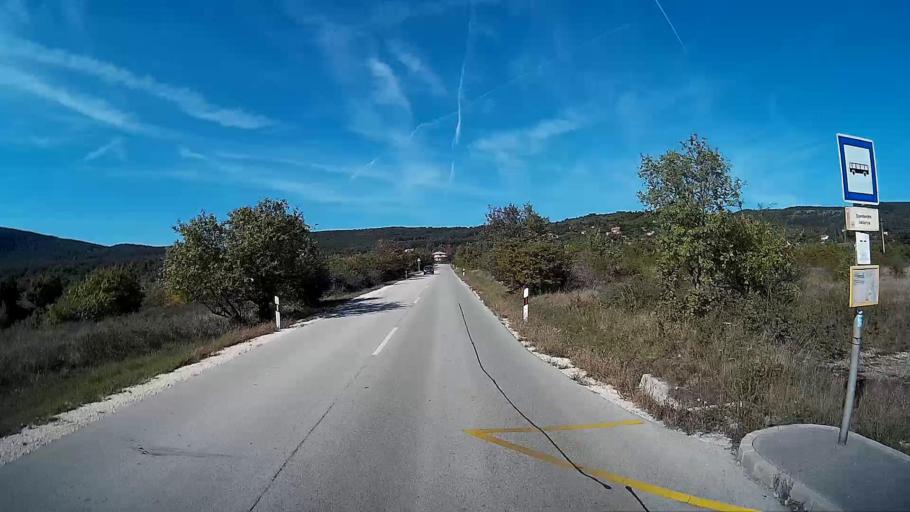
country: HU
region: Pest
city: Nagykovacsi
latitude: 47.6962
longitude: 19.0330
